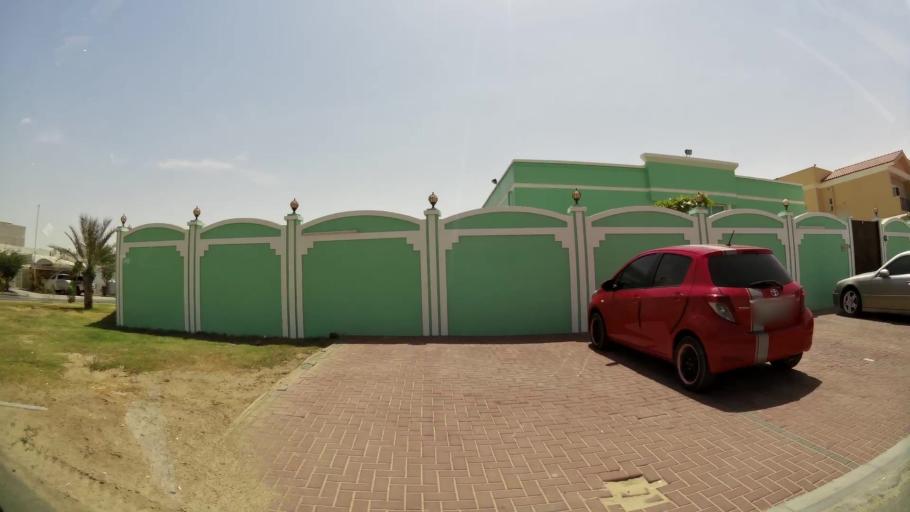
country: AE
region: Ash Shariqah
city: Sharjah
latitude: 25.1820
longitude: 55.4164
